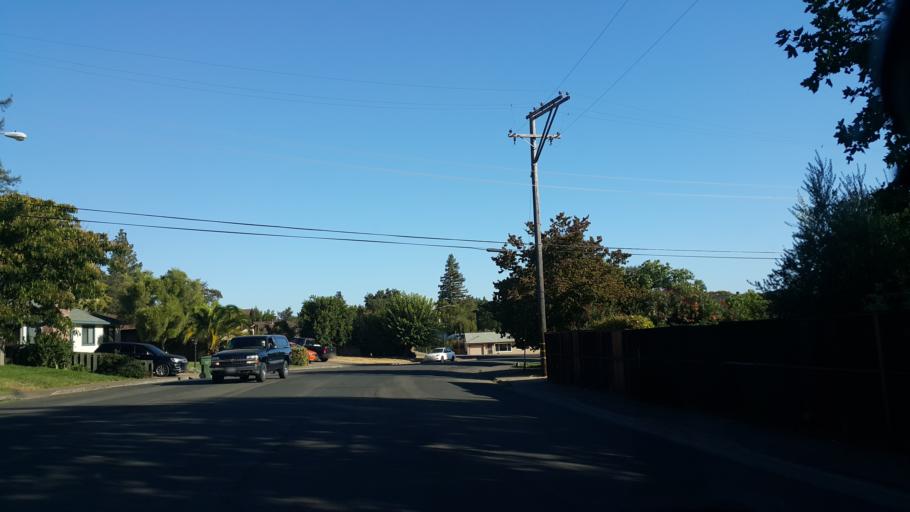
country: US
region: California
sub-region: Mendocino County
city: Ukiah
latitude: 39.1393
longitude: -123.2148
